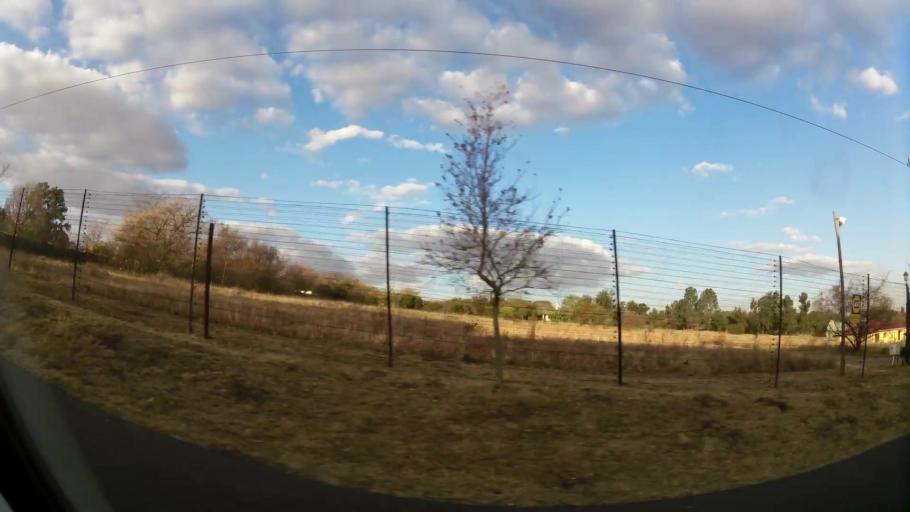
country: ZA
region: Gauteng
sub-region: City of Johannesburg Metropolitan Municipality
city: Diepsloot
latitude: -25.9970
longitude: 27.9684
